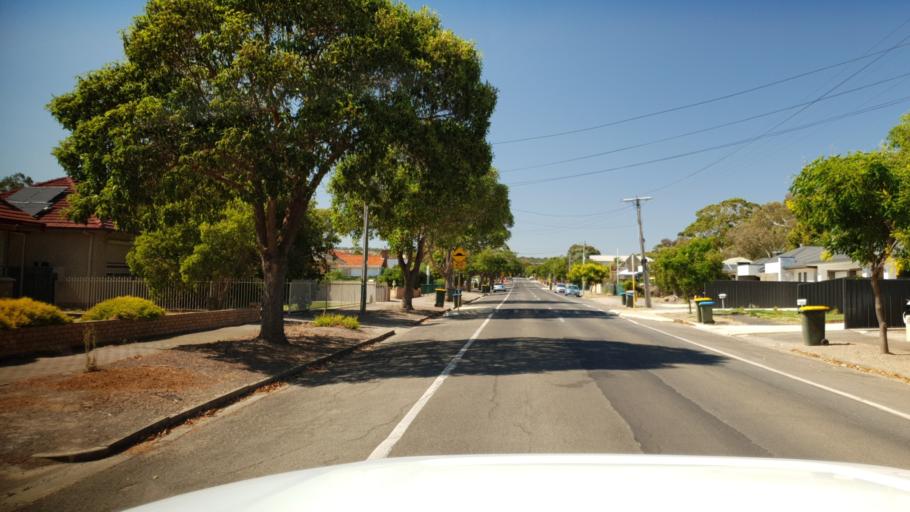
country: AU
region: South Australia
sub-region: Marion
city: Clovelly Park
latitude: -34.9966
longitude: 138.5789
